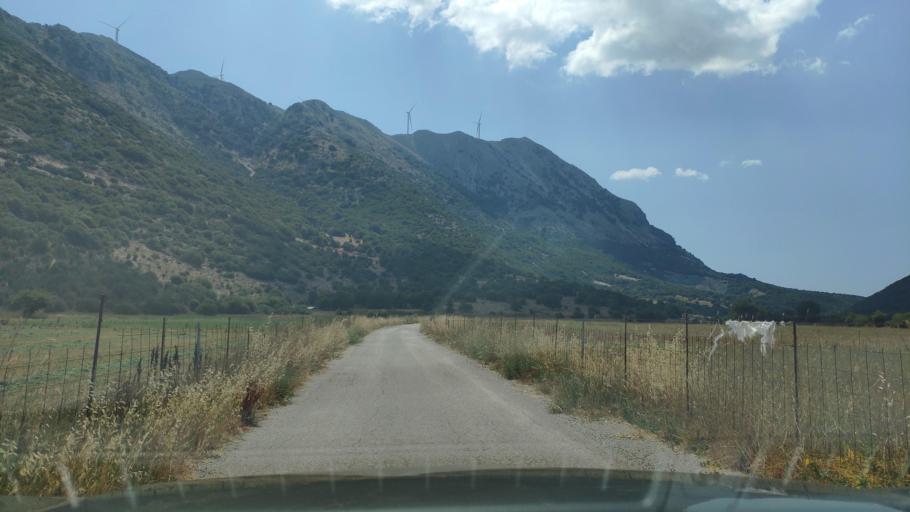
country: GR
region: West Greece
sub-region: Nomos Aitolias kai Akarnanias
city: Monastirakion
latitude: 38.7822
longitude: 20.9701
